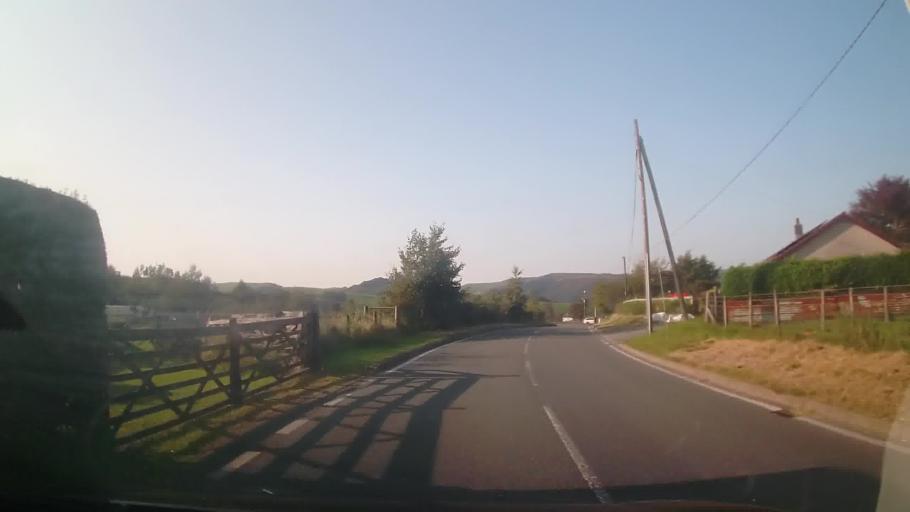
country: GB
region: Wales
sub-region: County of Ceredigion
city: Lledrod
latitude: 52.3702
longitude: -3.8570
